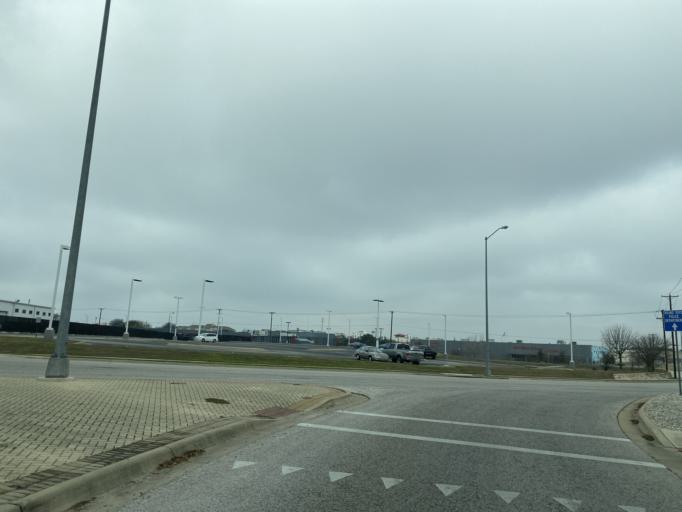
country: US
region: Texas
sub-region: Williamson County
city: Round Rock
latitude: 30.5362
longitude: -97.6880
